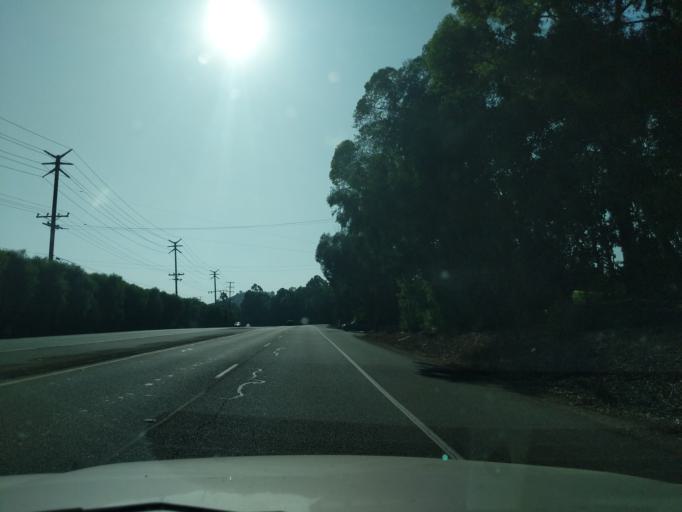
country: US
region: California
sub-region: Ventura County
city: Moorpark
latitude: 34.2687
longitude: -118.8450
